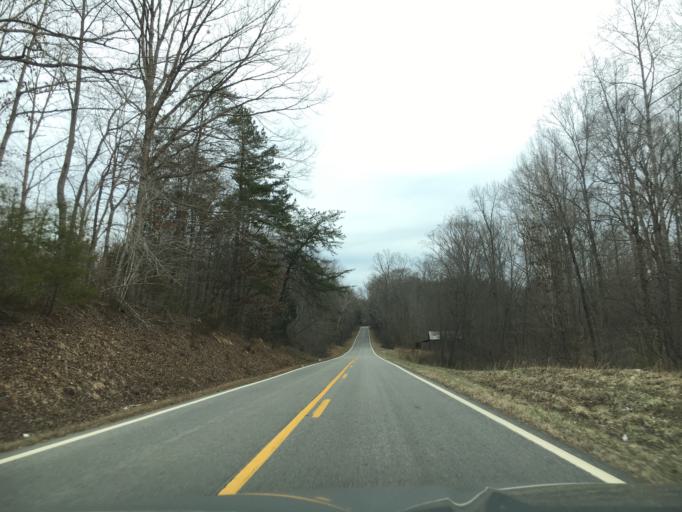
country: US
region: Virginia
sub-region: Charlotte County
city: Charlotte Court House
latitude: 37.1490
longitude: -78.7587
